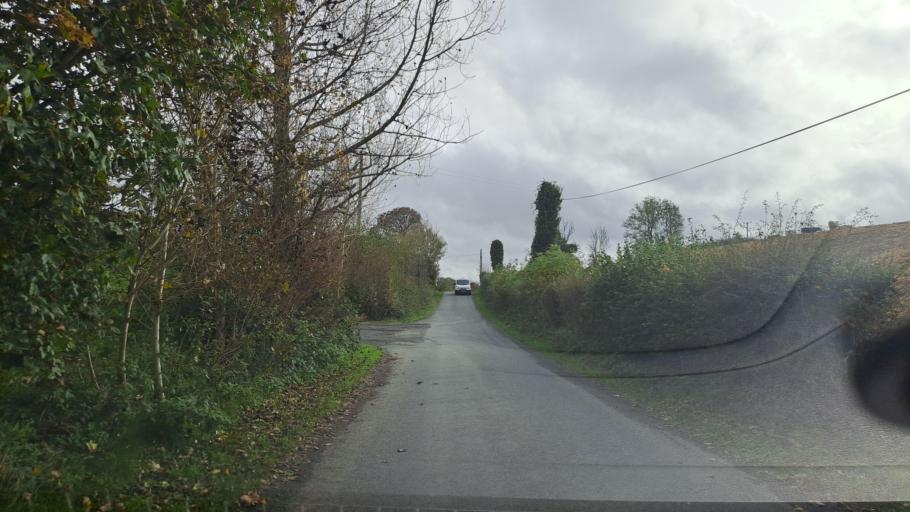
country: IE
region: Ulster
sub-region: An Cabhan
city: Bailieborough
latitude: 54.0167
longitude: -6.9004
